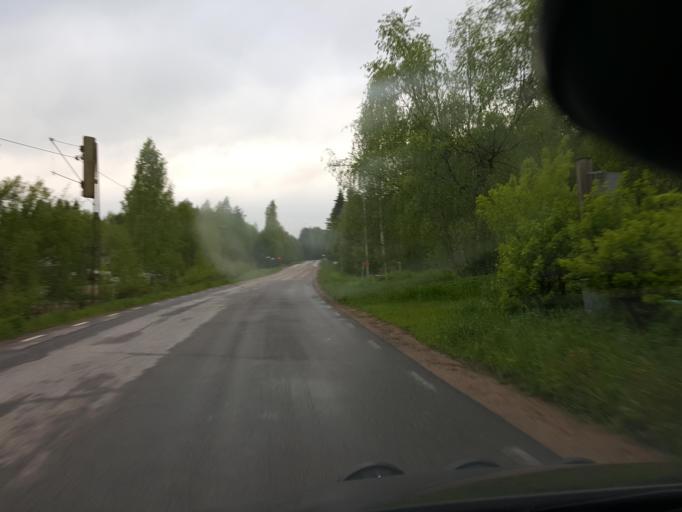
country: SE
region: Gaevleborg
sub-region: Ljusdals Kommun
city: Jaervsoe
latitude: 61.7991
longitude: 16.1818
